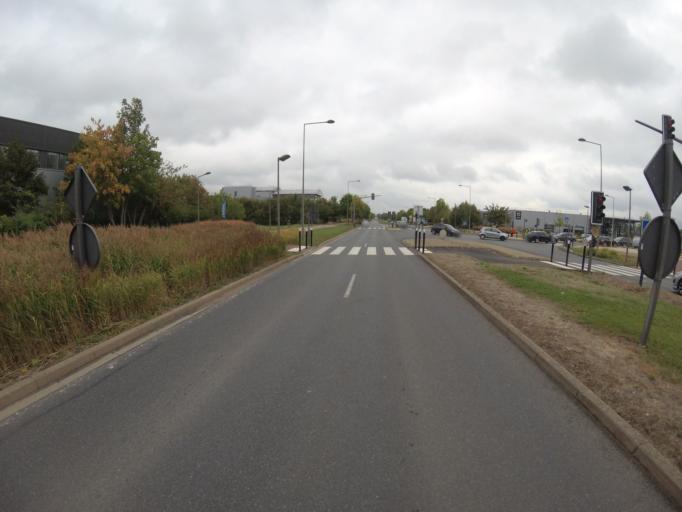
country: FR
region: Ile-de-France
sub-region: Departement de Seine-et-Marne
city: Chanteloup-en-Brie
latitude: 48.8547
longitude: 2.7584
